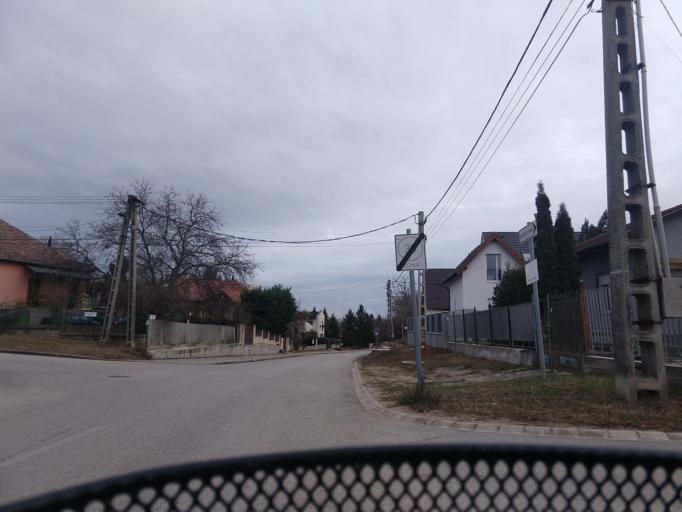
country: HU
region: Pest
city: Veresegyhaz
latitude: 47.6504
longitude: 19.2759
